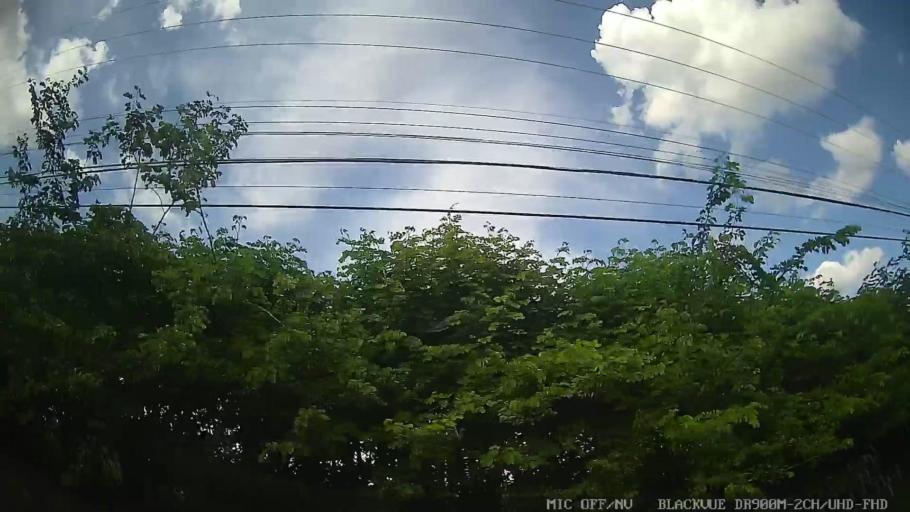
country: BR
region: Sao Paulo
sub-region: Jaguariuna
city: Jaguariuna
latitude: -22.6344
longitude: -47.0631
